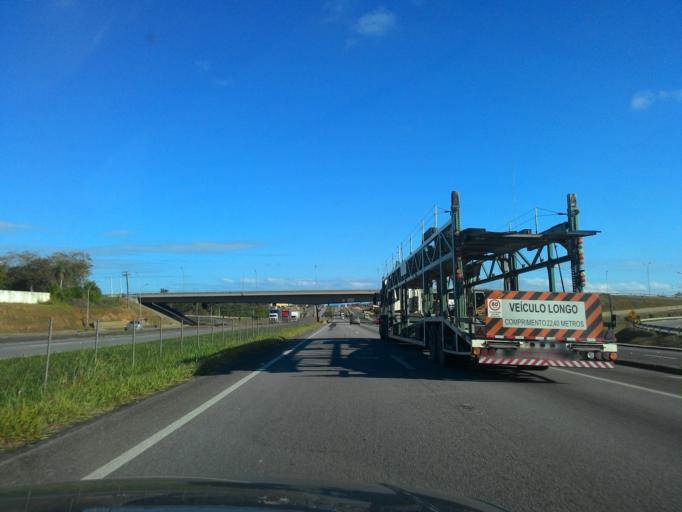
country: BR
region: Sao Paulo
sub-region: Registro
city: Registro
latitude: -24.5069
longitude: -47.8488
